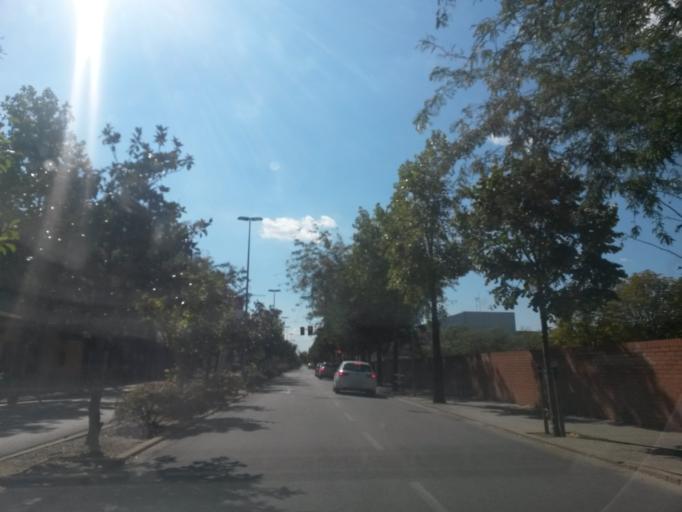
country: ES
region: Catalonia
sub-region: Provincia de Girona
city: Salt
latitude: 41.9710
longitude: 2.7865
